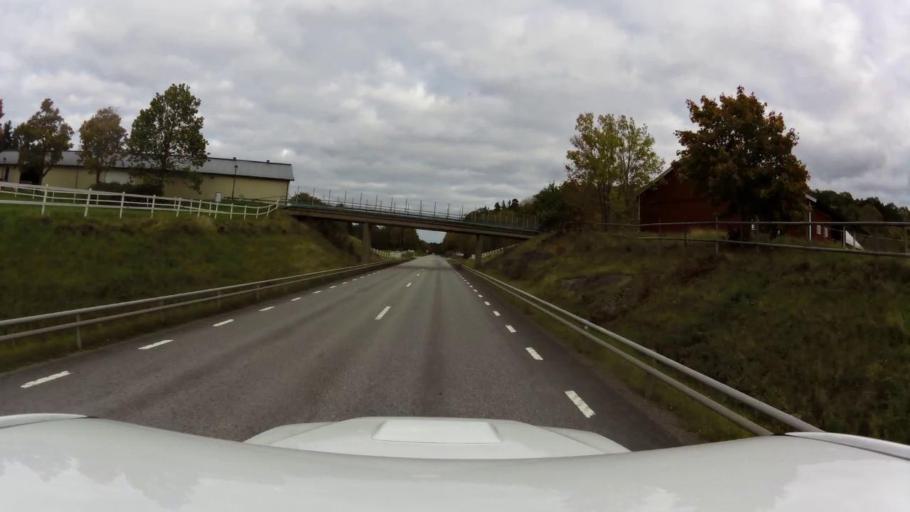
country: SE
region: OEstergoetland
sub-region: Kinda Kommun
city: Rimforsa
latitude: 58.1728
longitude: 15.6765
